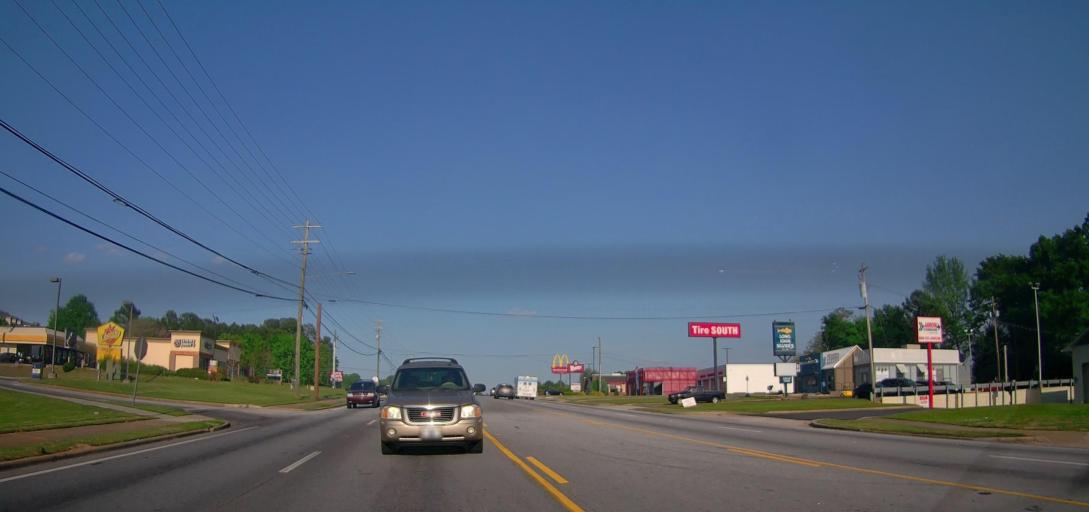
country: US
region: Georgia
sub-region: Newton County
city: Covington
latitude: 33.6031
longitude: -83.8551
